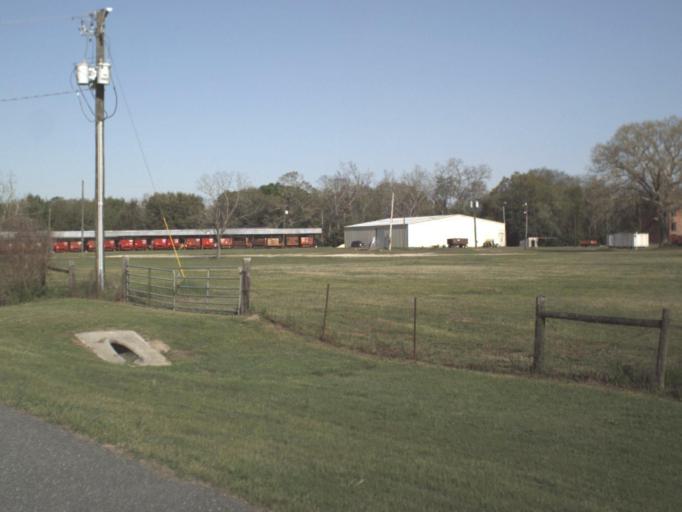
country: US
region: Florida
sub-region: Jackson County
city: Malone
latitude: 30.9573
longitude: -85.1568
